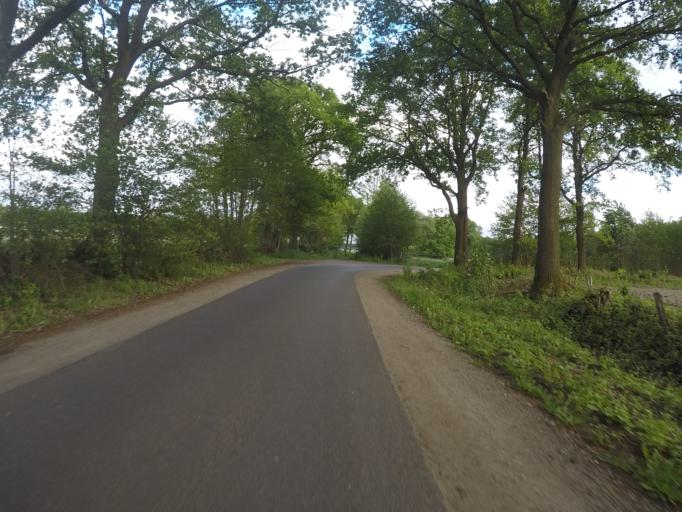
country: DE
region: Schleswig-Holstein
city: Bonningstedt
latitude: 53.6584
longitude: 9.9279
